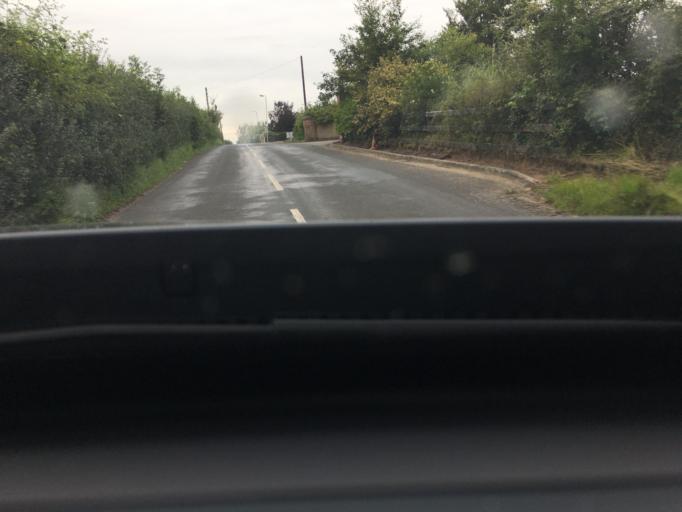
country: GB
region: Northern Ireland
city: Coalisland
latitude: 54.5370
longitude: -6.6187
